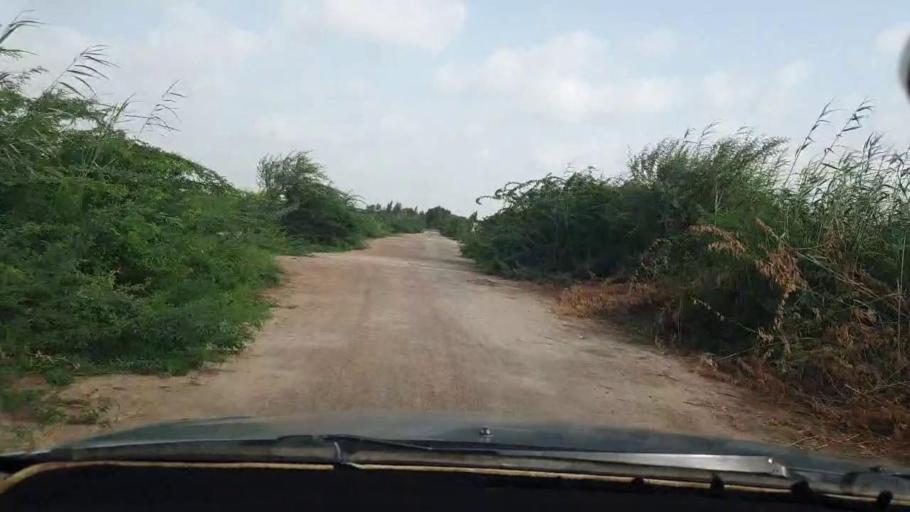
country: PK
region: Sindh
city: Tando Bago
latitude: 24.7790
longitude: 68.9827
